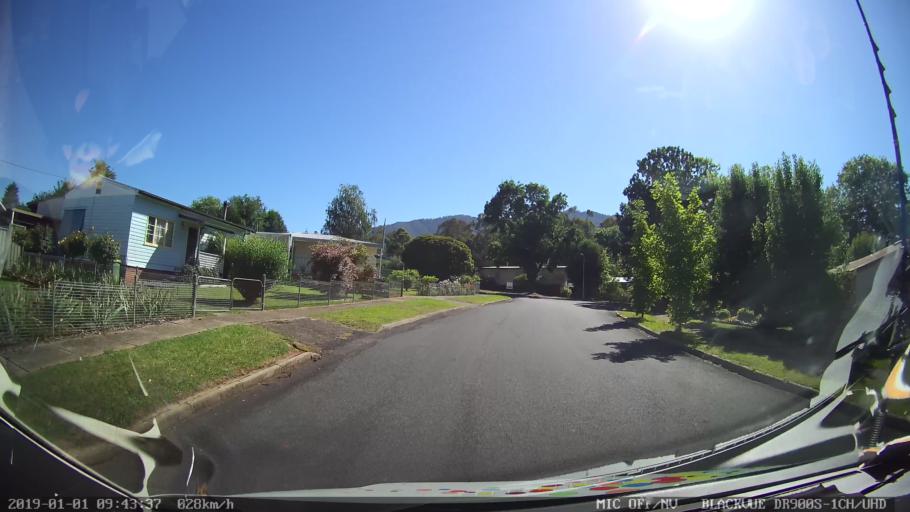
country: AU
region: New South Wales
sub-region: Snowy River
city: Jindabyne
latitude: -36.2146
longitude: 148.1350
